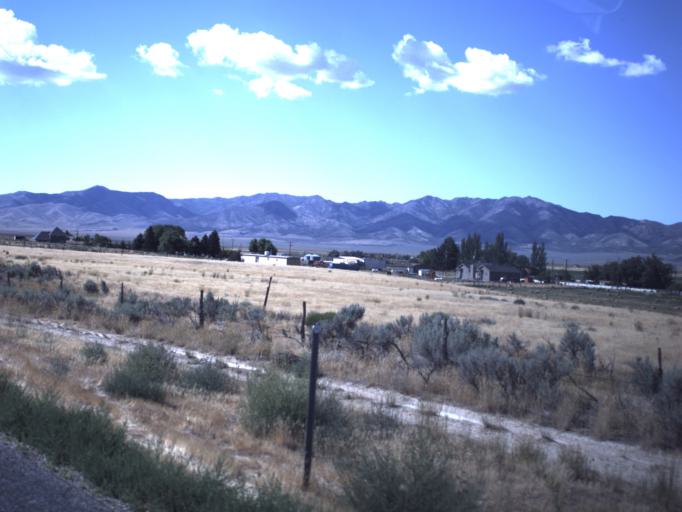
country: US
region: Utah
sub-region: Tooele County
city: Tooele
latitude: 40.0899
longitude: -112.4308
